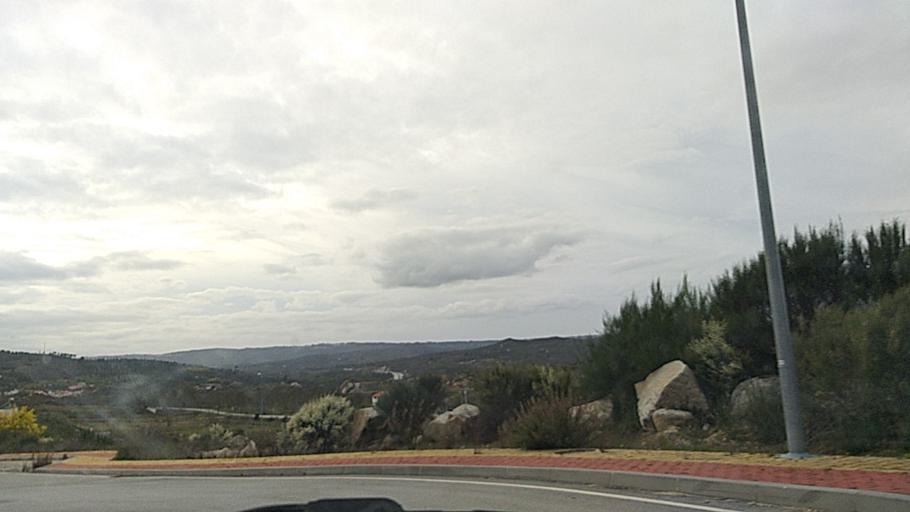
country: PT
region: Guarda
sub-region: Celorico da Beira
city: Celorico da Beira
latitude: 40.6270
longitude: -7.4174
